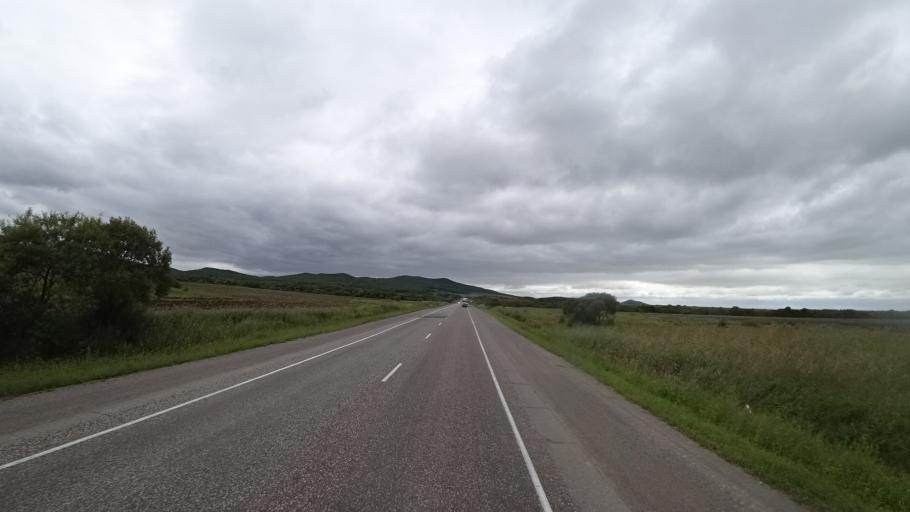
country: RU
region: Primorskiy
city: Chernigovka
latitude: 44.2862
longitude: 132.4998
